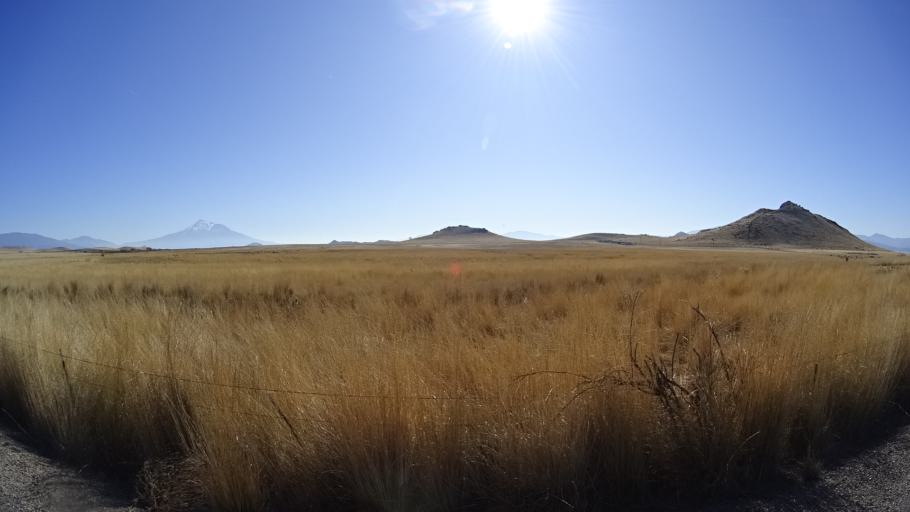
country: US
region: California
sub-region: Siskiyou County
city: Montague
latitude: 41.7565
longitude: -122.4805
